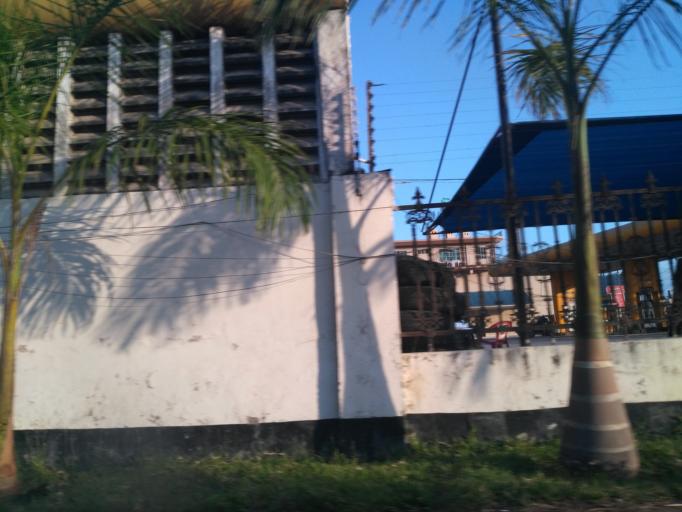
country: TZ
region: Dar es Salaam
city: Magomeni
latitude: -6.7665
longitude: 39.2611
